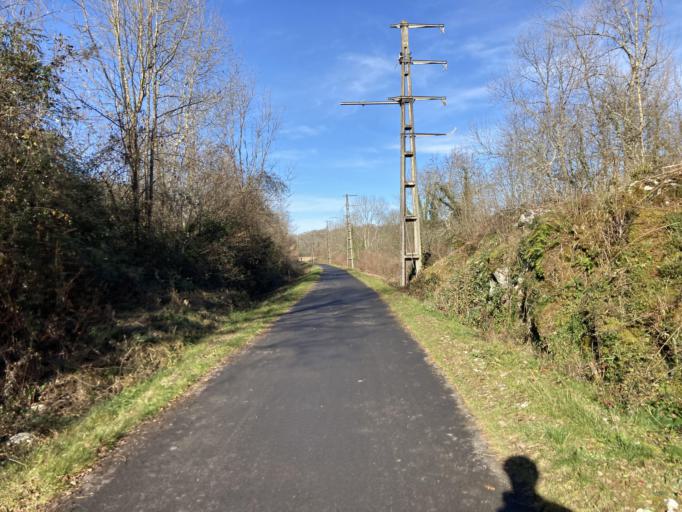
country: FR
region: Aquitaine
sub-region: Departement des Pyrenees-Atlantiques
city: Arudy
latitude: 43.1172
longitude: -0.4374
